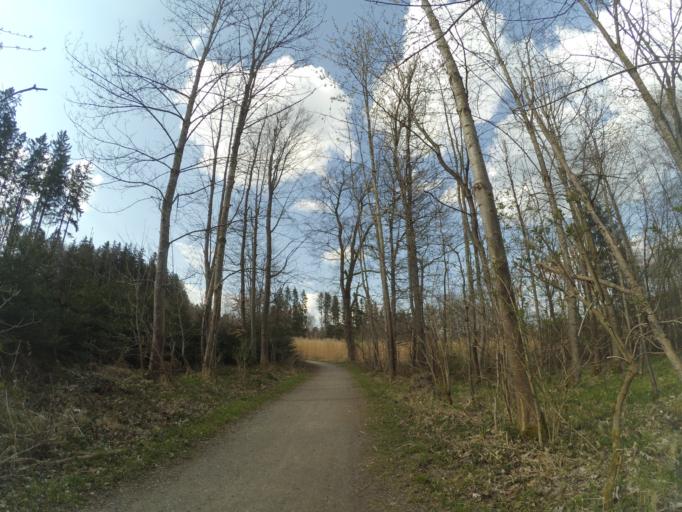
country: DE
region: Bavaria
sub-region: Swabia
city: Bad Worishofen
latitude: 48.0105
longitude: 10.5819
